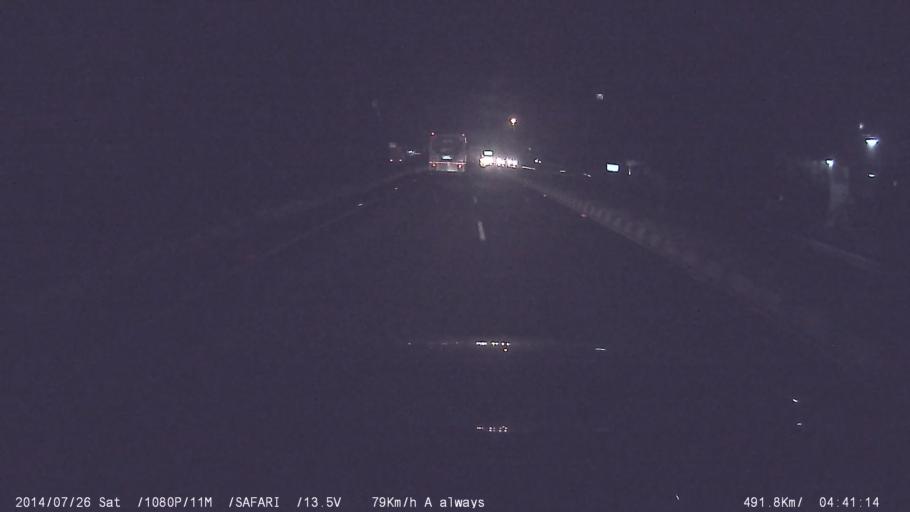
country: IN
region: Kerala
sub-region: Ernakulam
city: Angamali
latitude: 10.2139
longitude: 76.3798
